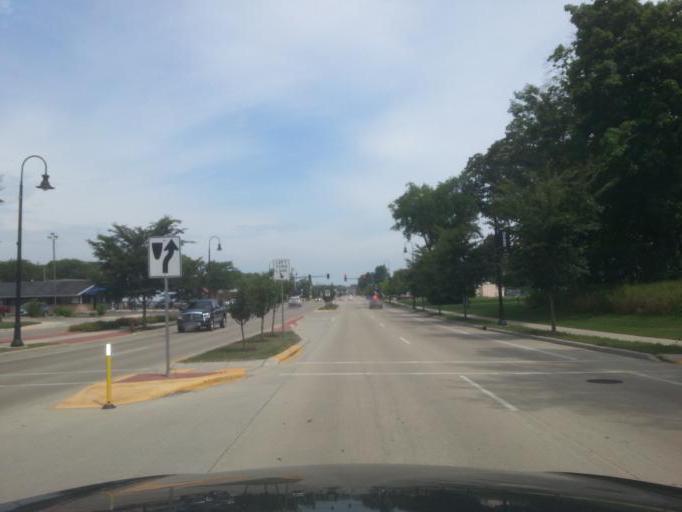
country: US
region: Wisconsin
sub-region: Dane County
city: Monona
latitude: 43.0556
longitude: -89.3255
